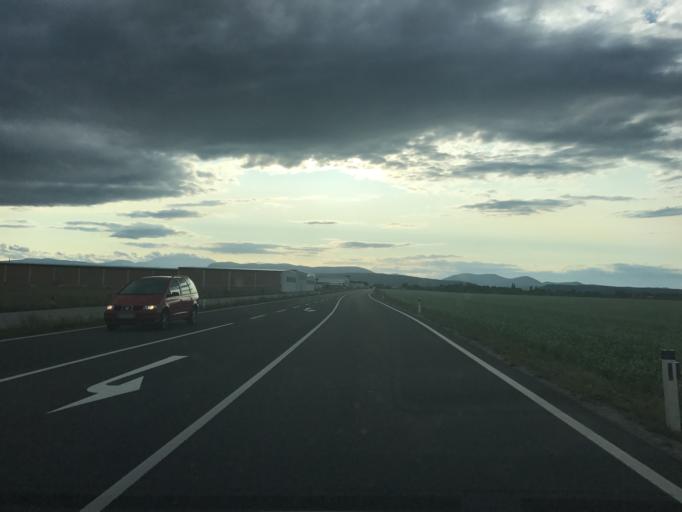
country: AT
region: Lower Austria
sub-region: Politischer Bezirk Wiener Neustadt
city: Lichtenworth
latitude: 47.8450
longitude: 16.2647
